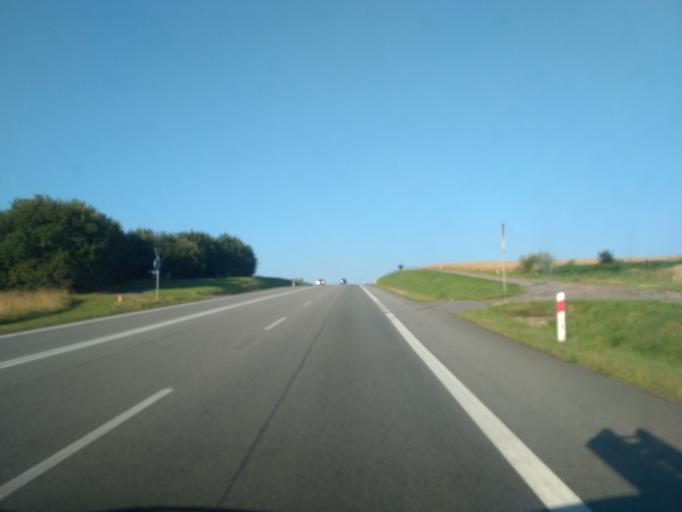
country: PL
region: Subcarpathian Voivodeship
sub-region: Powiat krosnienski
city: Miejsce Piastowe
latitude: 49.6120
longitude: 21.7458
